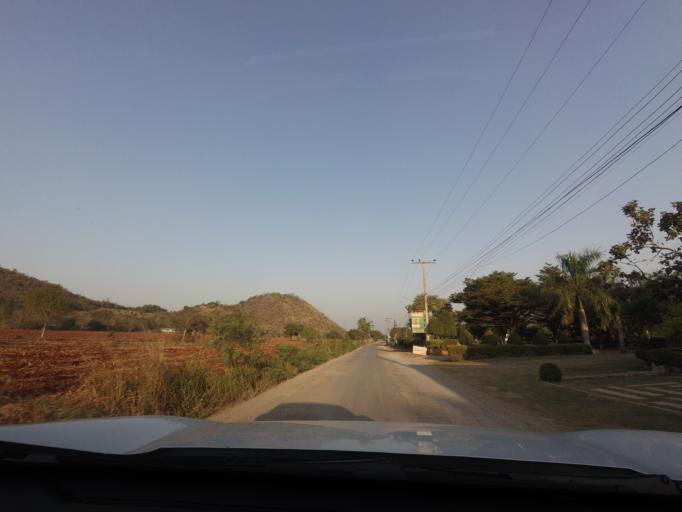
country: TH
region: Nakhon Ratchasima
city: Pak Chong
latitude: 14.6398
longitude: 101.3616
